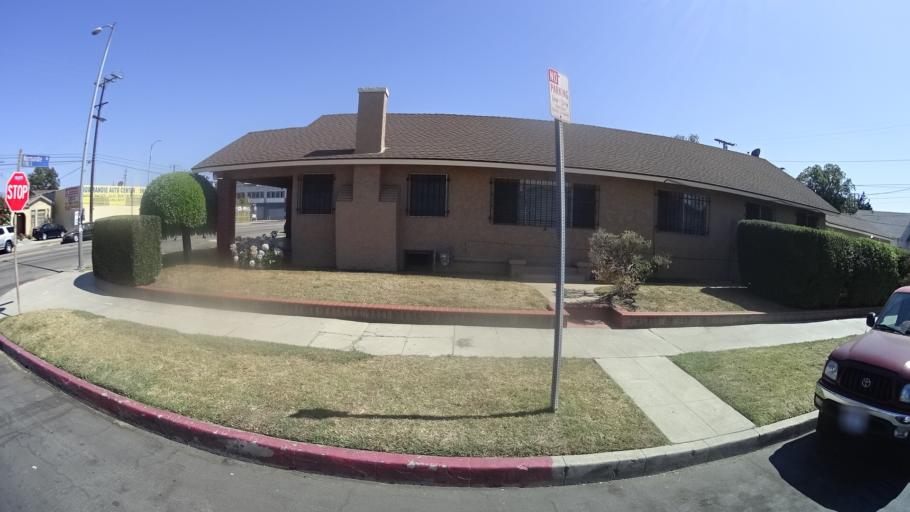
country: US
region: California
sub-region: Los Angeles County
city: View Park-Windsor Hills
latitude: 33.9905
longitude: -118.3005
